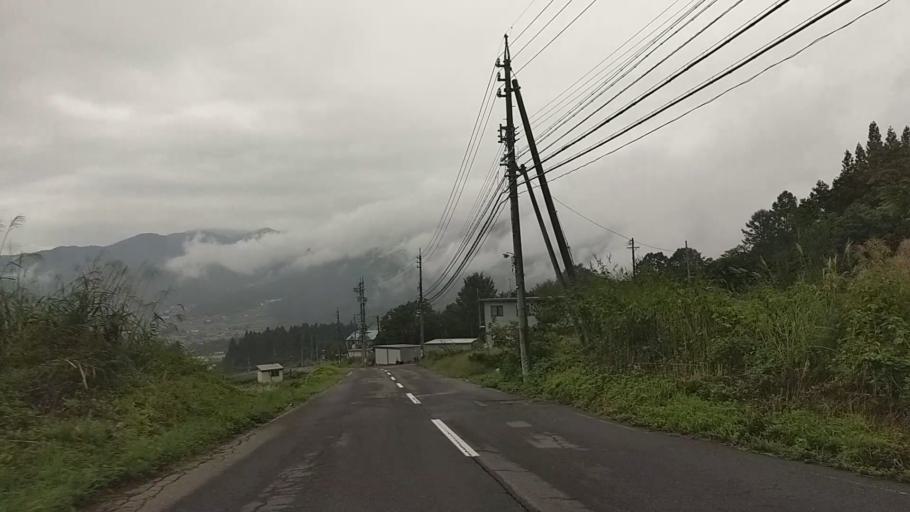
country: JP
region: Nagano
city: Iiyama
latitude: 36.8266
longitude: 138.3987
